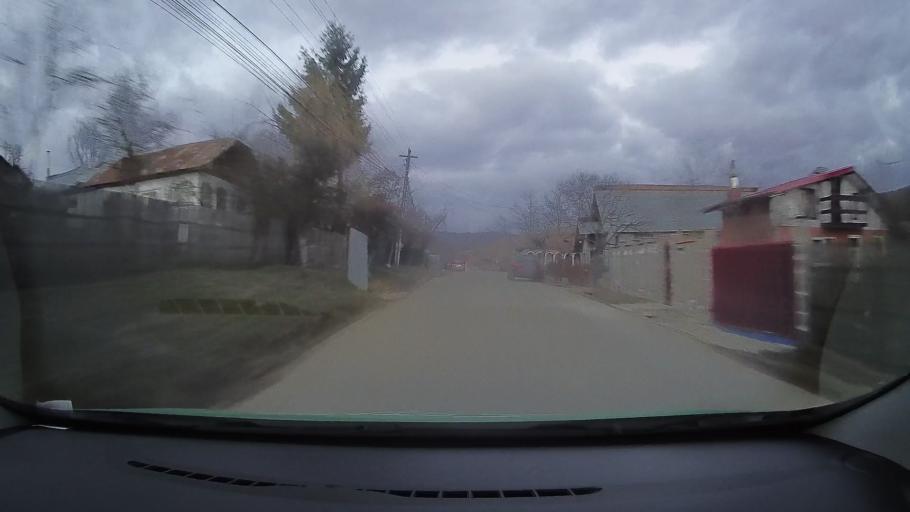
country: RO
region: Dambovita
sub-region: Comuna Visinesti
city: Visinesti
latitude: 45.1096
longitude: 25.5865
